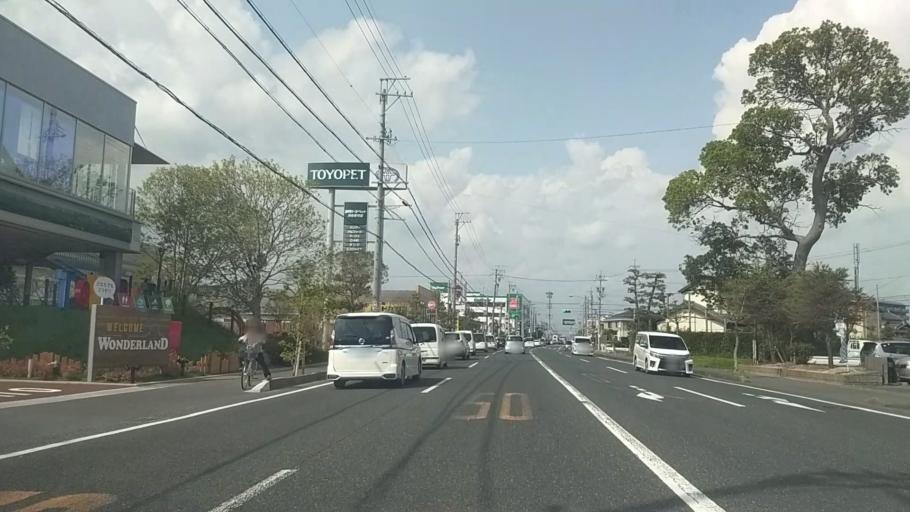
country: JP
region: Shizuoka
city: Hamamatsu
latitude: 34.7178
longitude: 137.7627
